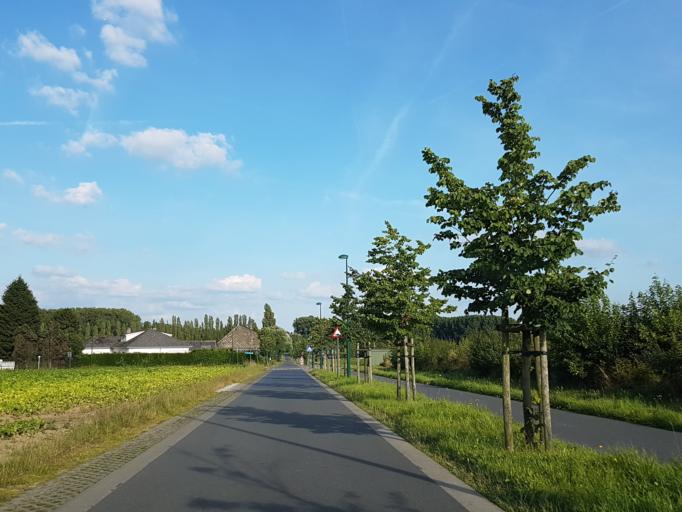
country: BE
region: Flanders
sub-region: Provincie Oost-Vlaanderen
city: Denderleeuw
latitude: 50.9311
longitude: 4.0996
